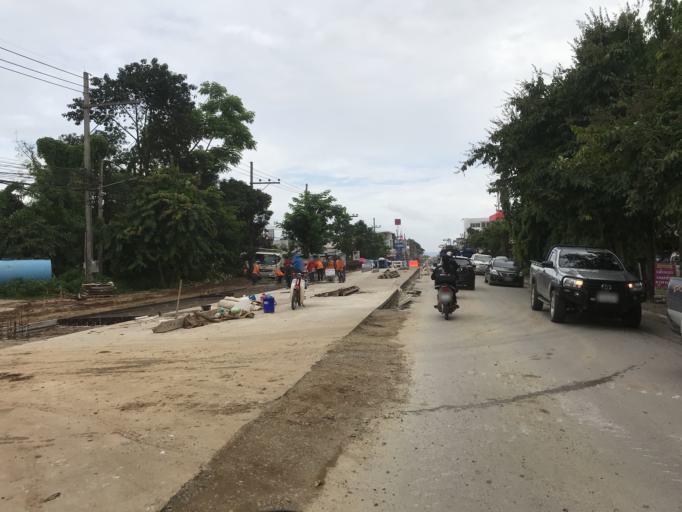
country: TH
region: Chiang Rai
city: Chiang Rai
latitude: 19.8969
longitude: 99.8319
